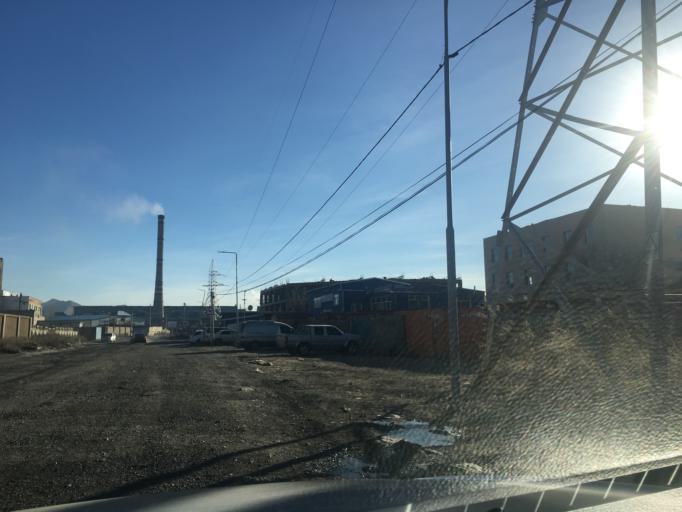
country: MN
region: Ulaanbaatar
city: Ulaanbaatar
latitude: 47.9062
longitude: 106.8028
